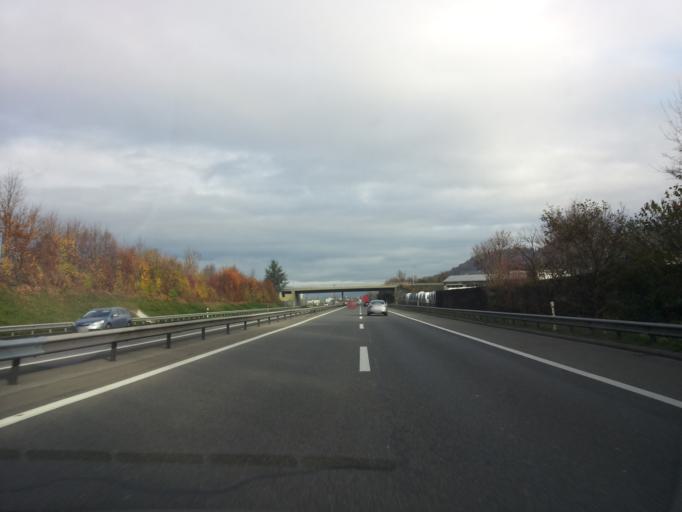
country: CH
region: Lucerne
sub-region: Willisau District
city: Dagmersellen
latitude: 47.2180
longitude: 7.9748
